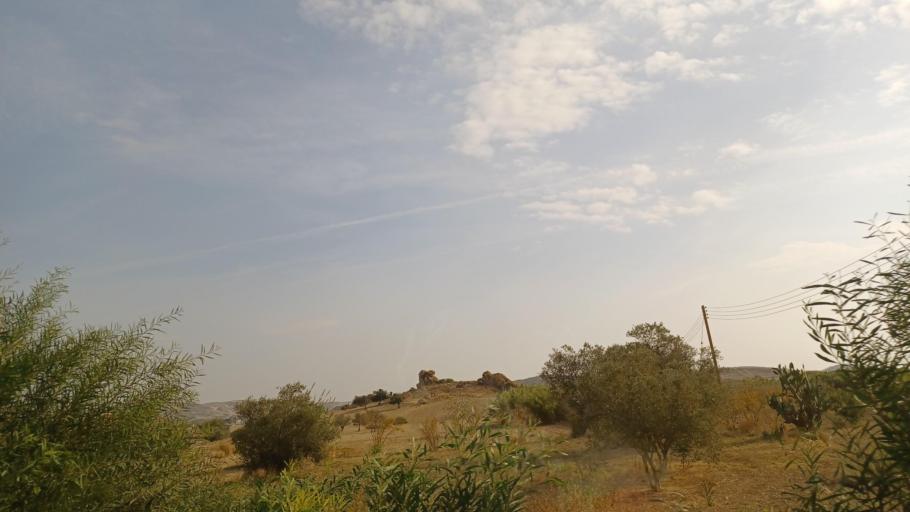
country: CY
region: Larnaka
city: Troulloi
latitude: 35.0274
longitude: 33.6059
